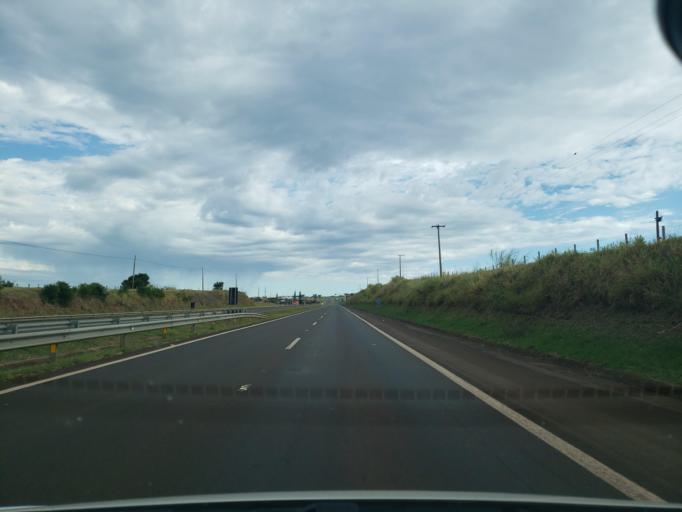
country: BR
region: Sao Paulo
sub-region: Jau
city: Jau
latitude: -22.2615
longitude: -48.5343
